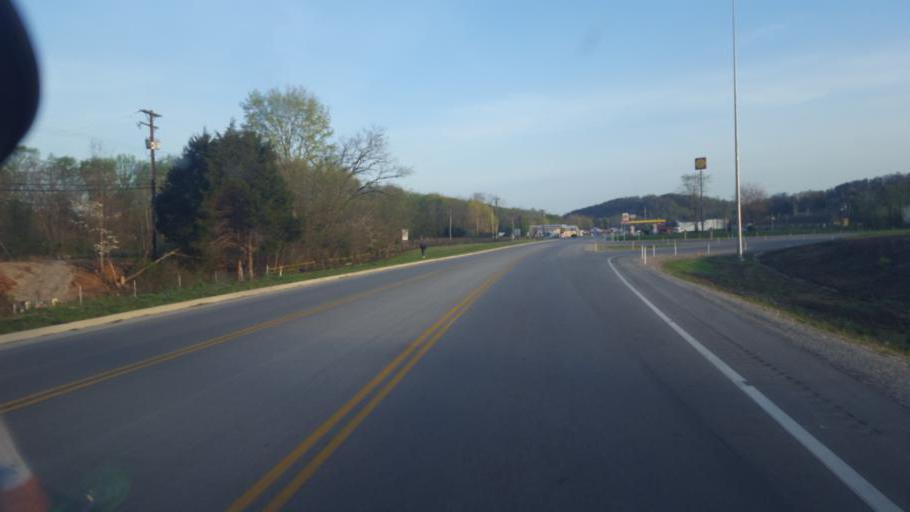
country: US
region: Kentucky
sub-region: Hart County
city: Munfordville
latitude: 37.2922
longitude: -85.9042
